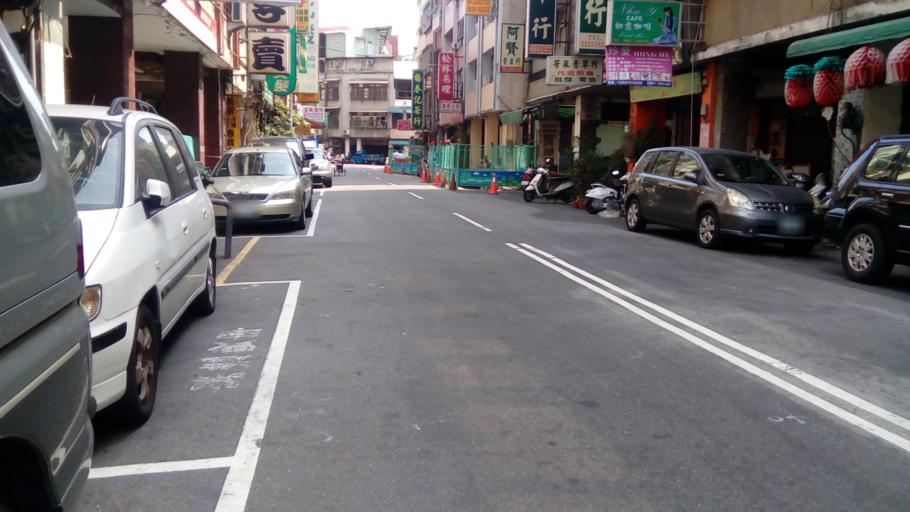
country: TW
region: Taiwan
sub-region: Taichung City
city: Taichung
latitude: 24.1407
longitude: 120.6846
